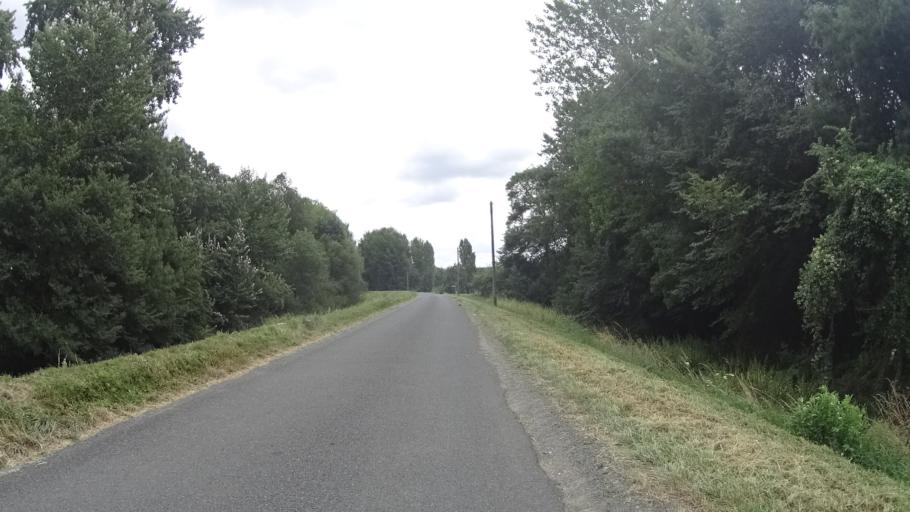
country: FR
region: Centre
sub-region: Departement d'Indre-et-Loire
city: Huismes
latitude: 47.2603
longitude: 0.2804
